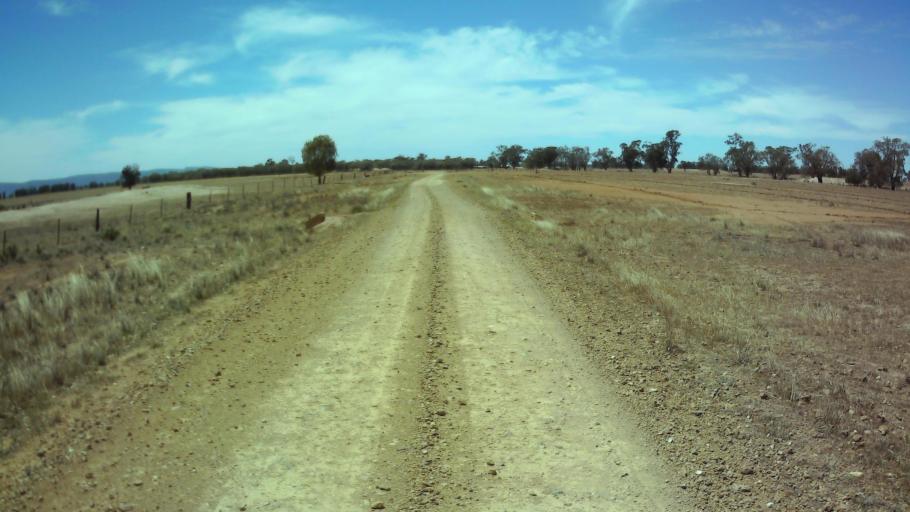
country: AU
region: New South Wales
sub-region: Weddin
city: Grenfell
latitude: -33.8645
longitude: 147.7614
